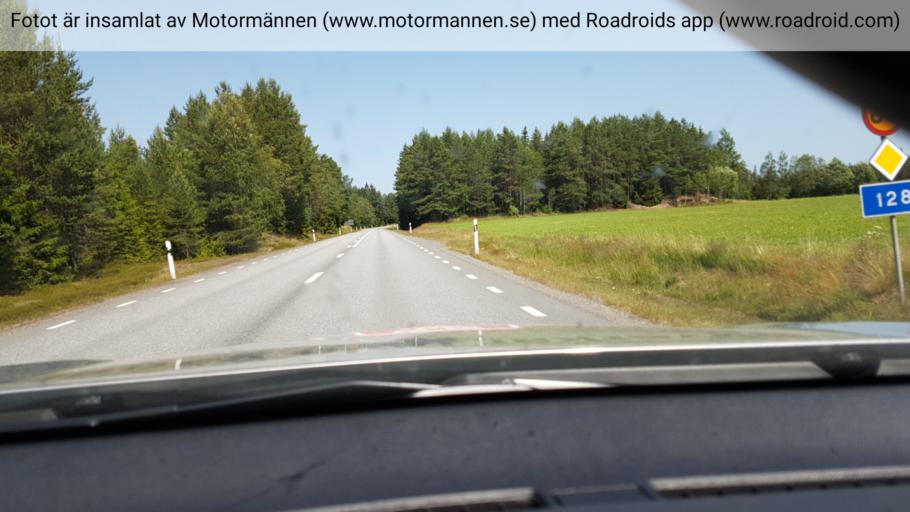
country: SE
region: Joenkoeping
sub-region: Savsjo Kommun
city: Saevsjoe
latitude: 57.4287
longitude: 14.6967
